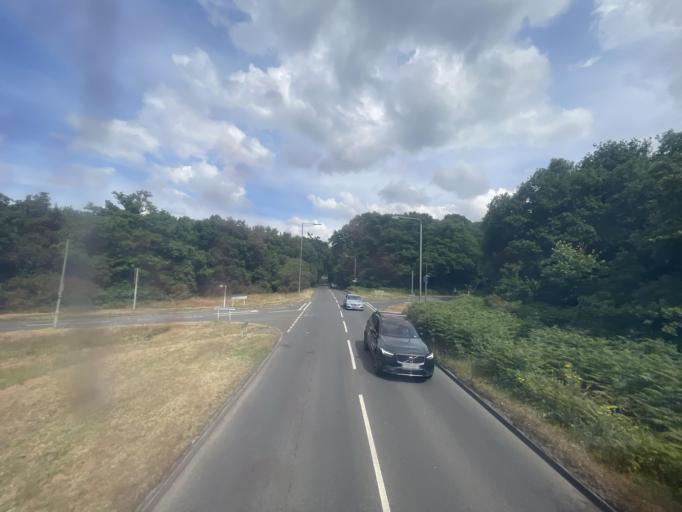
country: GB
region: England
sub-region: Greater London
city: West Wickham
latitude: 51.3673
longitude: 0.0199
